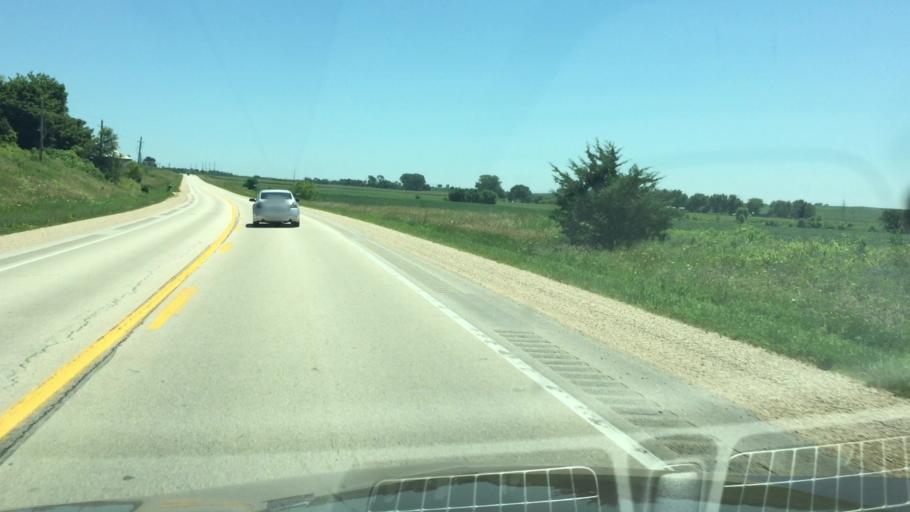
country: US
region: Iowa
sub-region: Jackson County
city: Maquoketa
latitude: 42.0698
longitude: -90.7929
